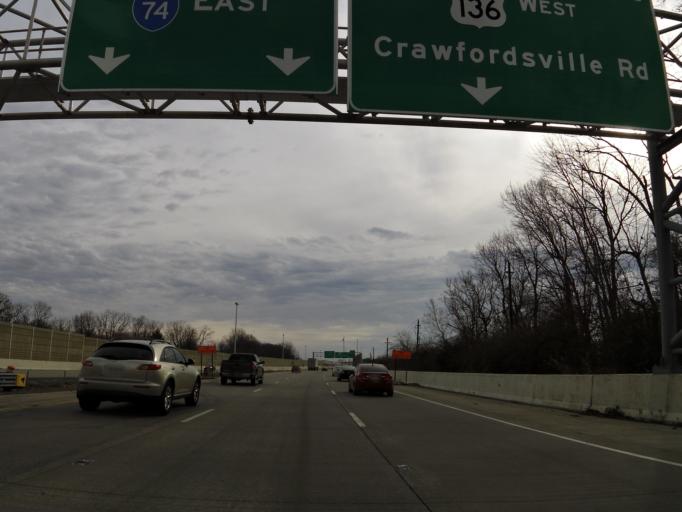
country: US
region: Indiana
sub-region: Marion County
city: Speedway
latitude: 39.8108
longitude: -86.2850
